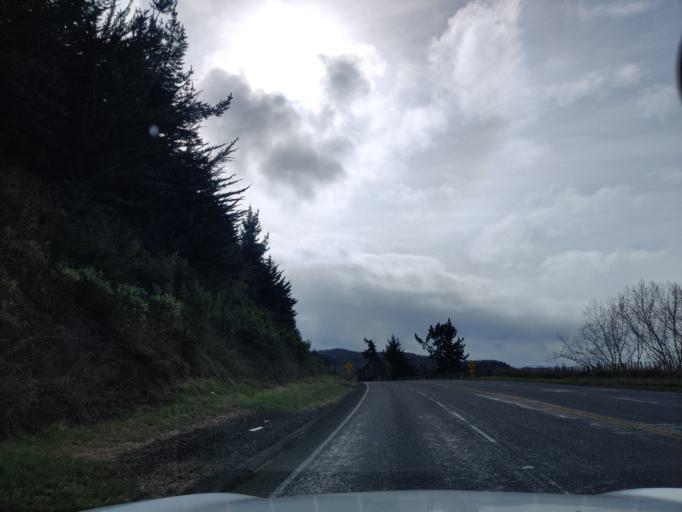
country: NZ
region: Manawatu-Wanganui
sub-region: Ruapehu District
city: Waiouru
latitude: -39.7696
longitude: 175.7984
